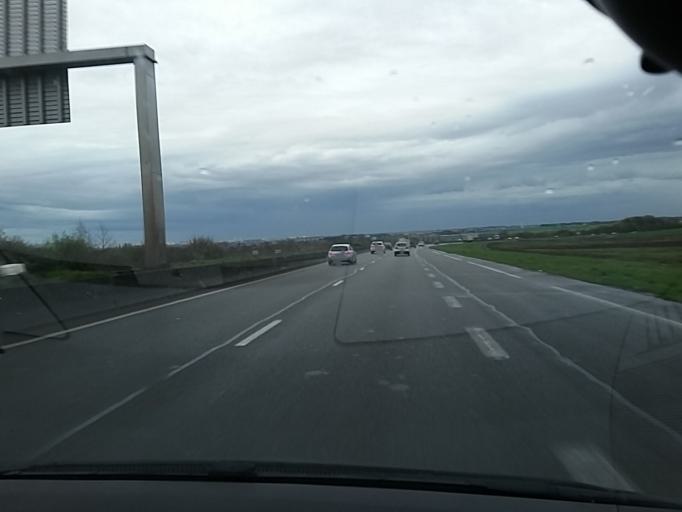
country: FR
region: Picardie
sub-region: Departement de la Somme
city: Longueau
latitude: 49.8715
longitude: 2.3720
